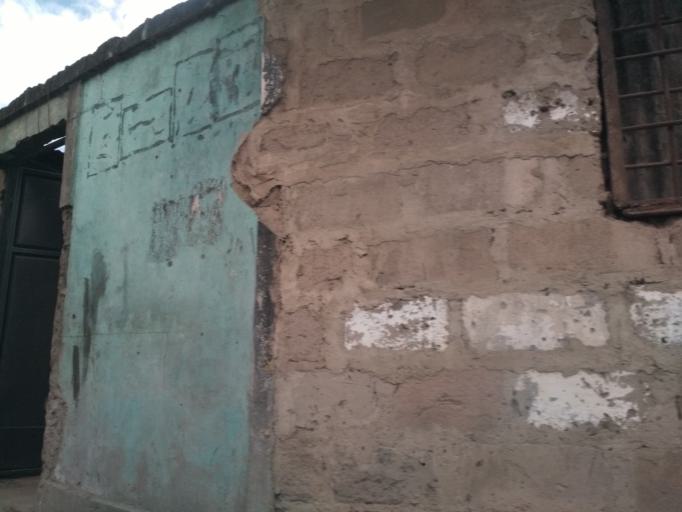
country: TZ
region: Dar es Salaam
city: Magomeni
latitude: -6.8031
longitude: 39.2656
